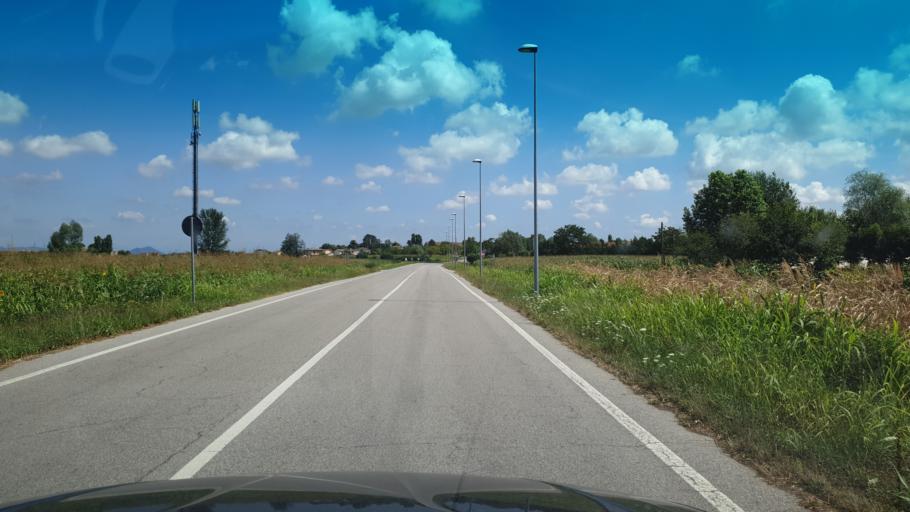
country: IT
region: Veneto
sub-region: Provincia di Rovigo
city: Costa di Rovigo
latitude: 45.0523
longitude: 11.6910
